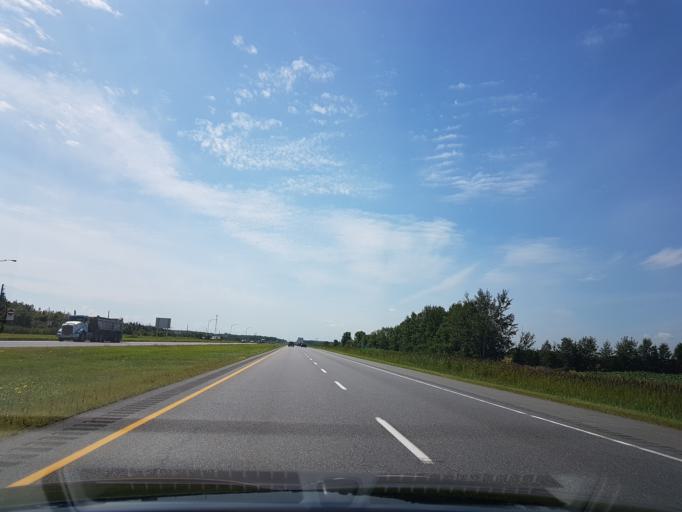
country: CA
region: Quebec
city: Les Cedres
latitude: 45.3345
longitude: -74.1025
